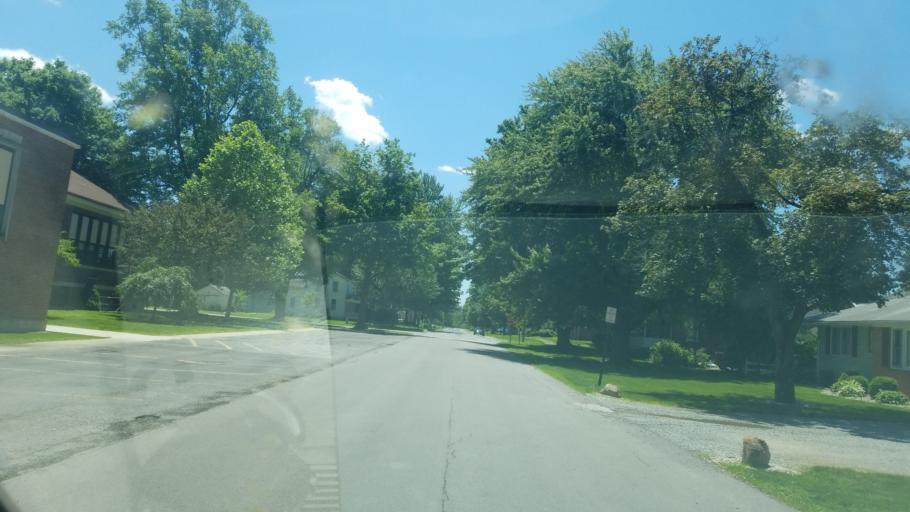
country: US
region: Ohio
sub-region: Wyandot County
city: Upper Sandusky
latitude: 40.8324
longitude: -83.2767
